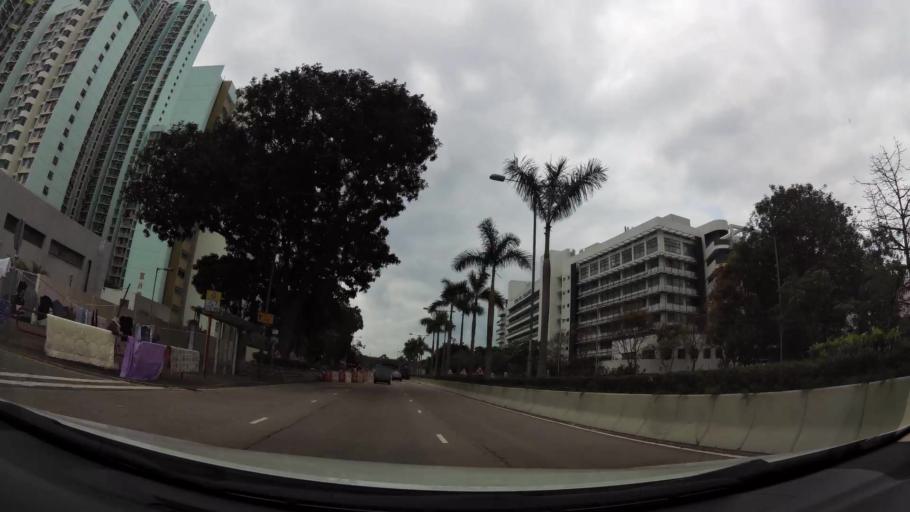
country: HK
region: Sham Shui Po
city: Sham Shui Po
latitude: 22.3303
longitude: 114.1538
